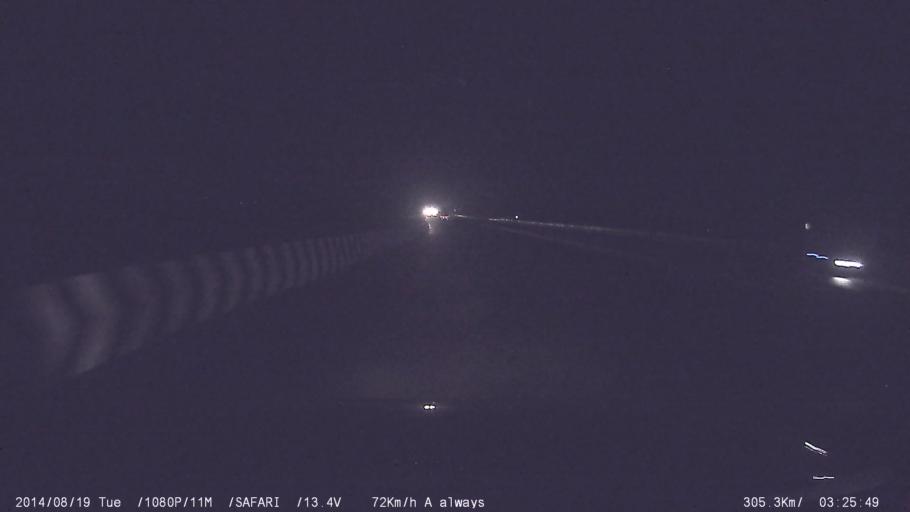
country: IN
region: Tamil Nadu
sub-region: Tiruppur
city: Avinashi
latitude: 11.1760
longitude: 77.2548
